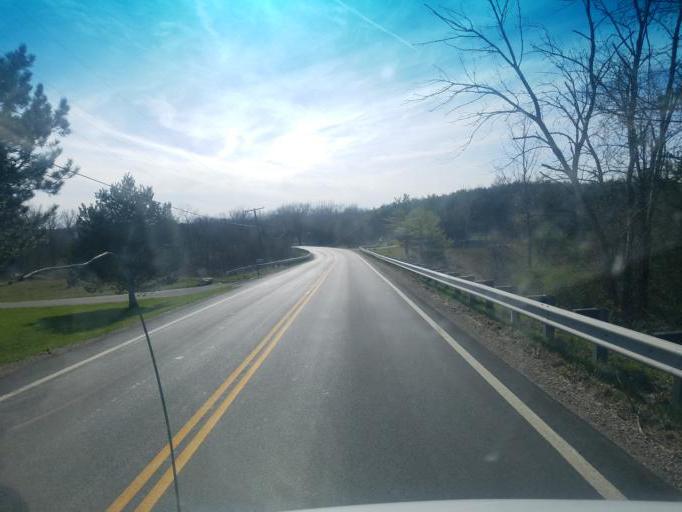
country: US
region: Ohio
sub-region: Union County
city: Marysville
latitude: 40.3351
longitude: -83.4472
